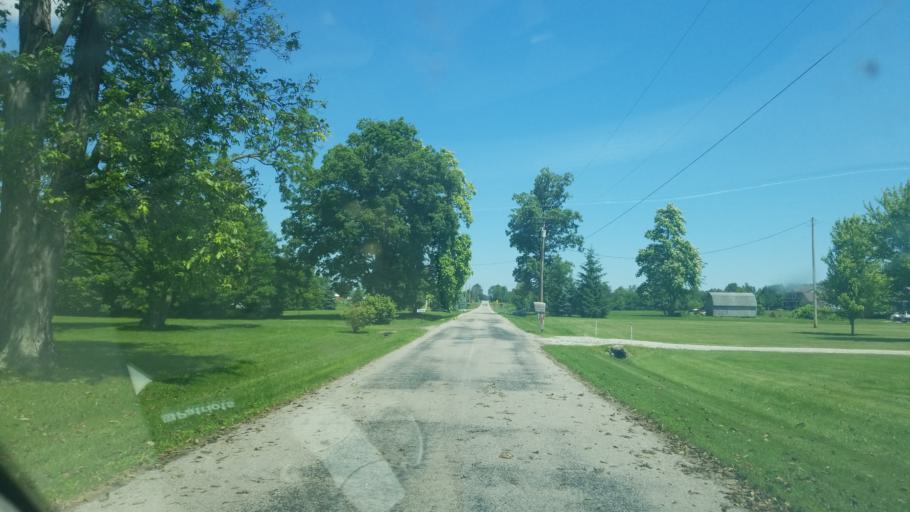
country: US
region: Ohio
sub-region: Huron County
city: Wakeman
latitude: 41.1836
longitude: -82.3902
